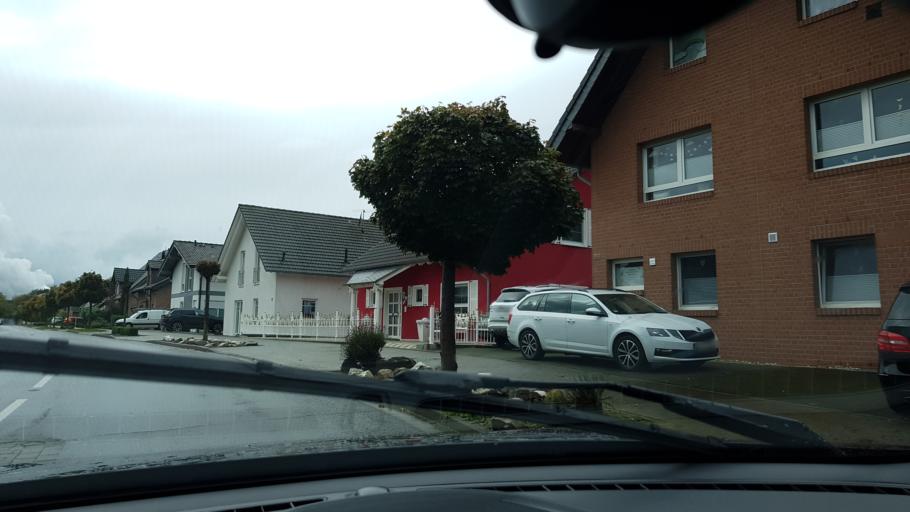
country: DE
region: North Rhine-Westphalia
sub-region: Regierungsbezirk Dusseldorf
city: Rommerskirchen
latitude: 51.0678
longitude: 6.6655
